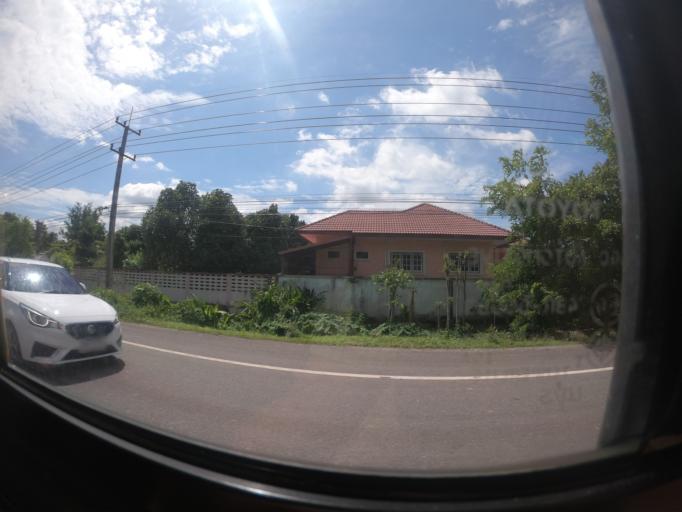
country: TH
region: Nakhon Nayok
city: Nakhon Nayok
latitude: 14.2802
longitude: 101.2960
